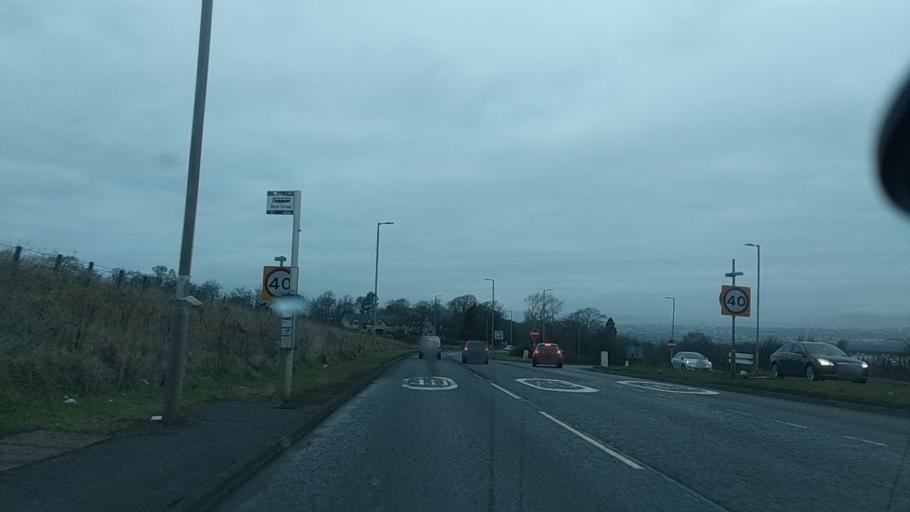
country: GB
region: Scotland
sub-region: South Lanarkshire
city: East Kilbride
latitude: 55.8016
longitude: -4.1786
